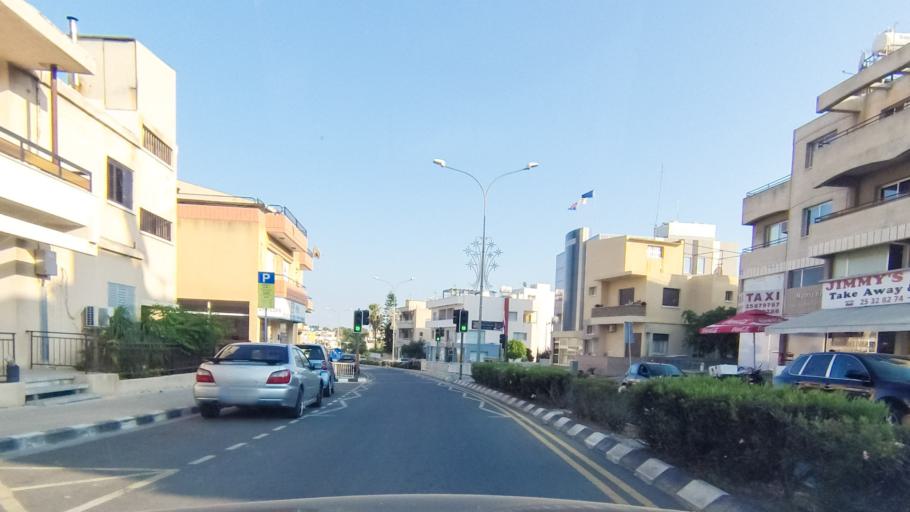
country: CY
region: Limassol
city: Mouttagiaka
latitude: 34.7054
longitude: 33.0864
